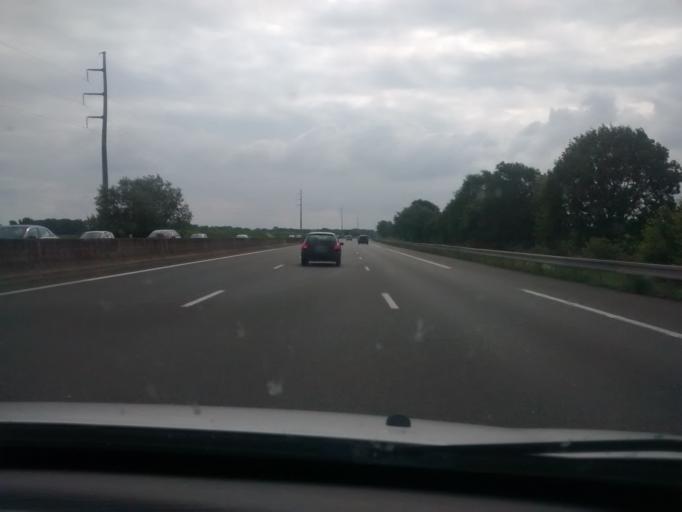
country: FR
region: Centre
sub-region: Departement d'Eure-et-Loir
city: Bailleau-le-Pin
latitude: 48.2891
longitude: 1.2640
